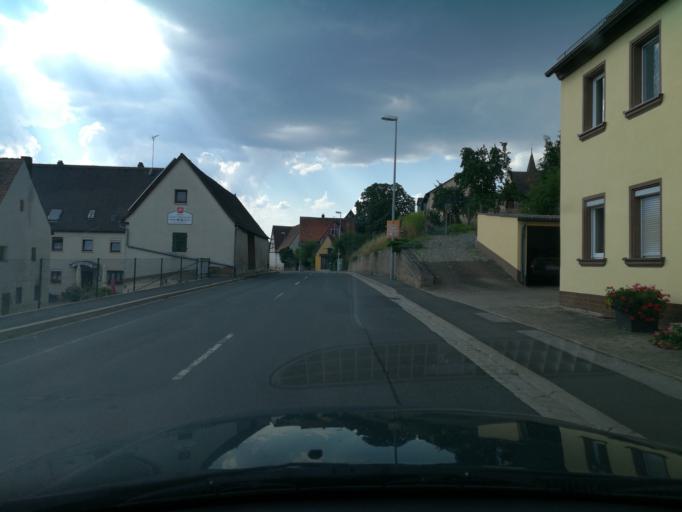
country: DE
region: Bavaria
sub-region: Regierungsbezirk Mittelfranken
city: Grosshabersdorf
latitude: 49.4094
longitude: 10.7648
